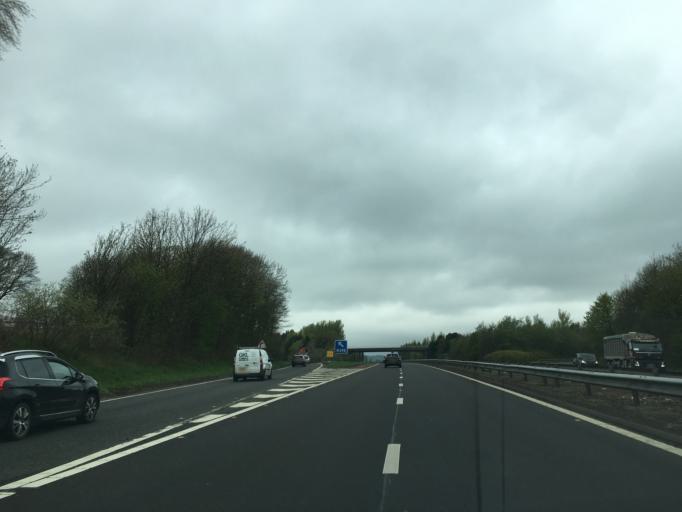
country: GB
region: Scotland
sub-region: Renfrewshire
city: Bishopton
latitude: 55.8977
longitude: -4.4831
